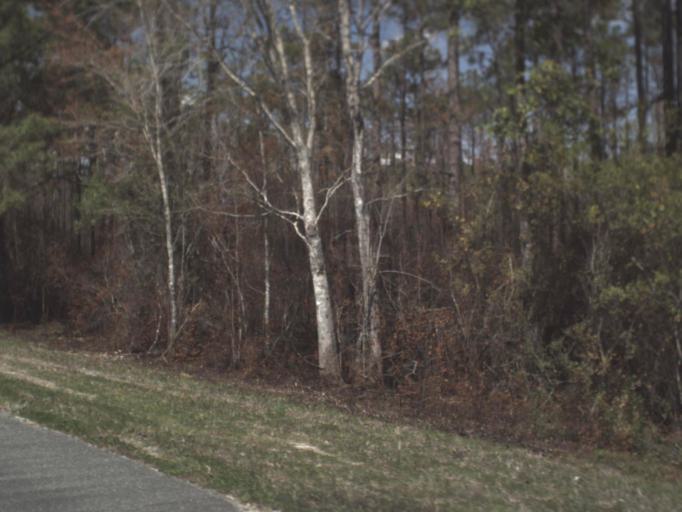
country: US
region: Florida
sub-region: Gadsden County
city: Midway
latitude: 30.3695
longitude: -84.5470
